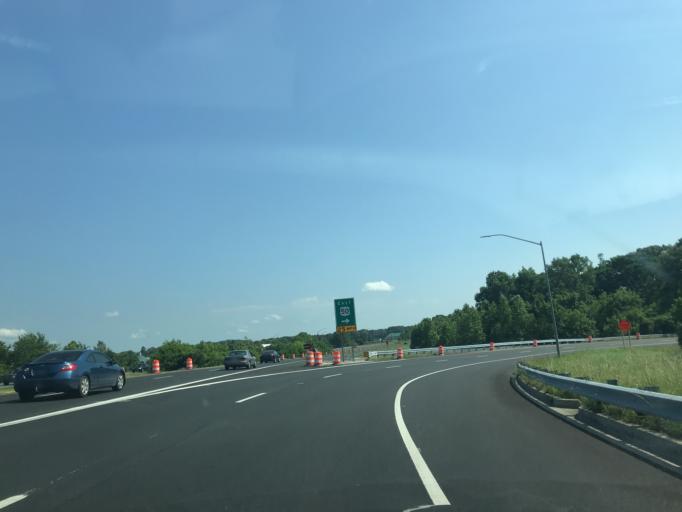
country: US
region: Maryland
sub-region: Wicomico County
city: Salisbury
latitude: 38.3681
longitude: -75.5374
